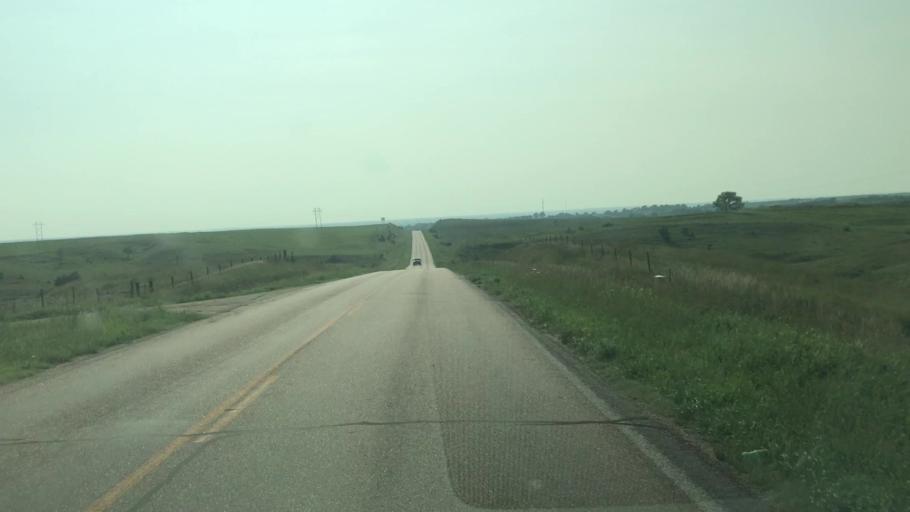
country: US
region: Nebraska
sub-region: Sherman County
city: Loup City
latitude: 41.2793
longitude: -98.9347
